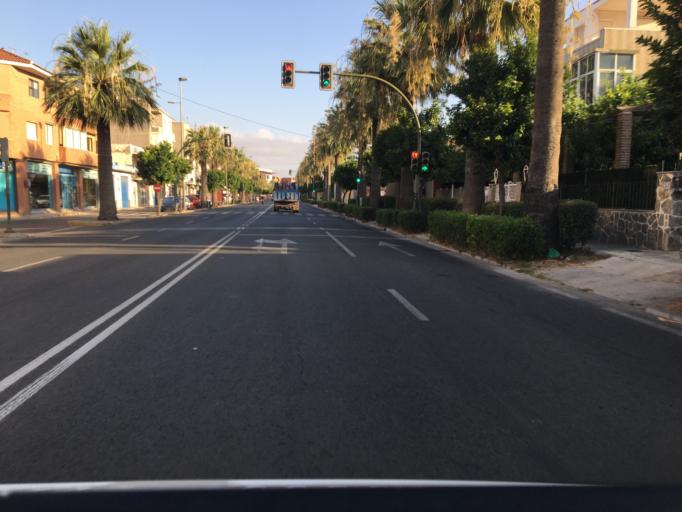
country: ES
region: Murcia
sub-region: Murcia
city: Cartagena
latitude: 37.6239
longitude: -0.9996
